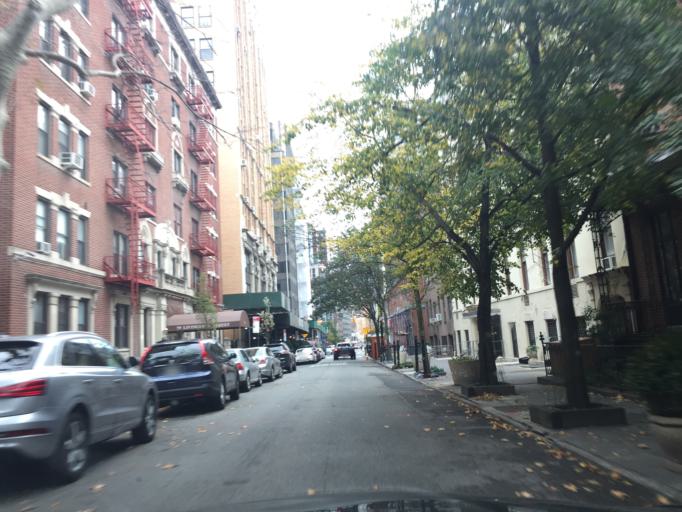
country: US
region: New York
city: New York City
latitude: 40.6919
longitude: -73.9925
